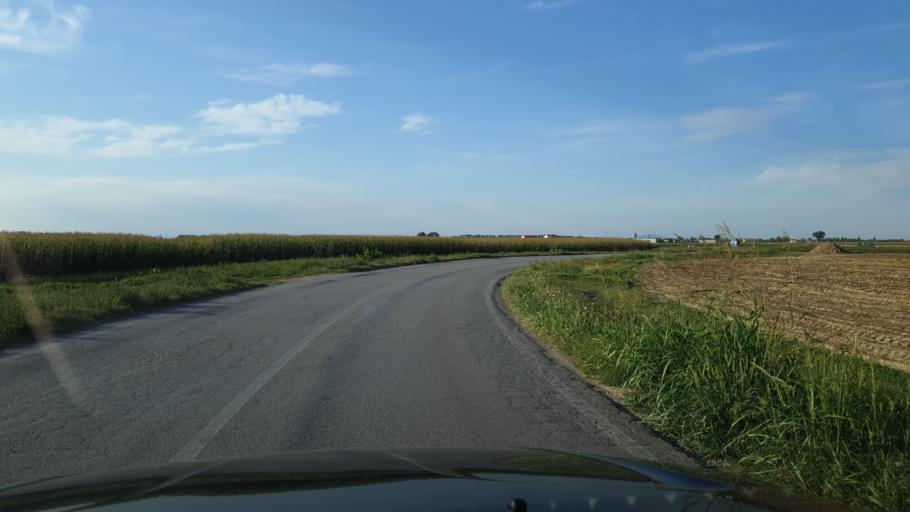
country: IT
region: Veneto
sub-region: Provincia di Rovigo
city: Fiesso Umbertiano
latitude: 44.9750
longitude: 11.6078
